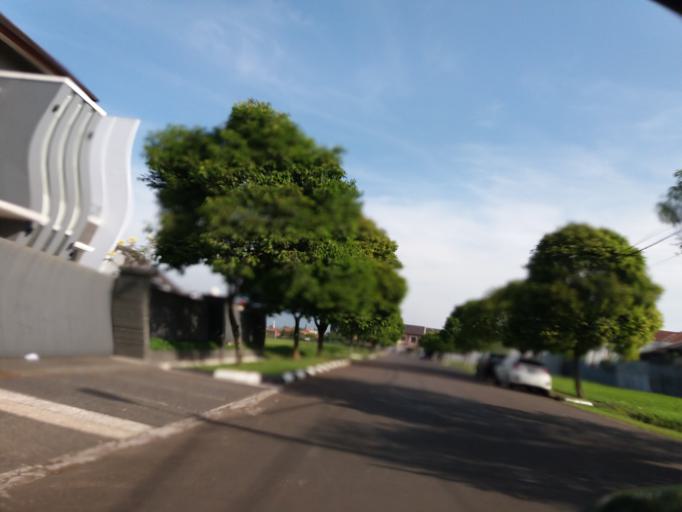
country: ID
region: West Java
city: Bandung
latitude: -6.9588
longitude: 107.6336
